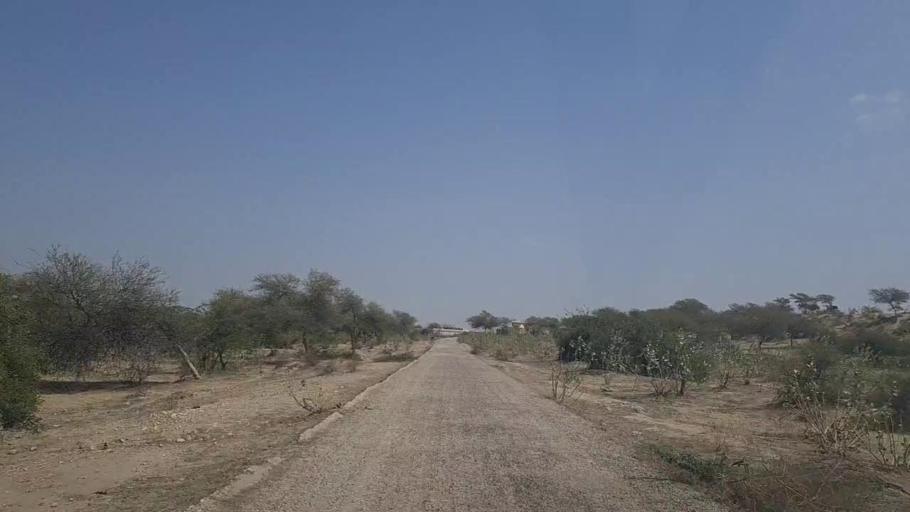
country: PK
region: Sindh
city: Naukot
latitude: 24.8184
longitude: 69.5031
